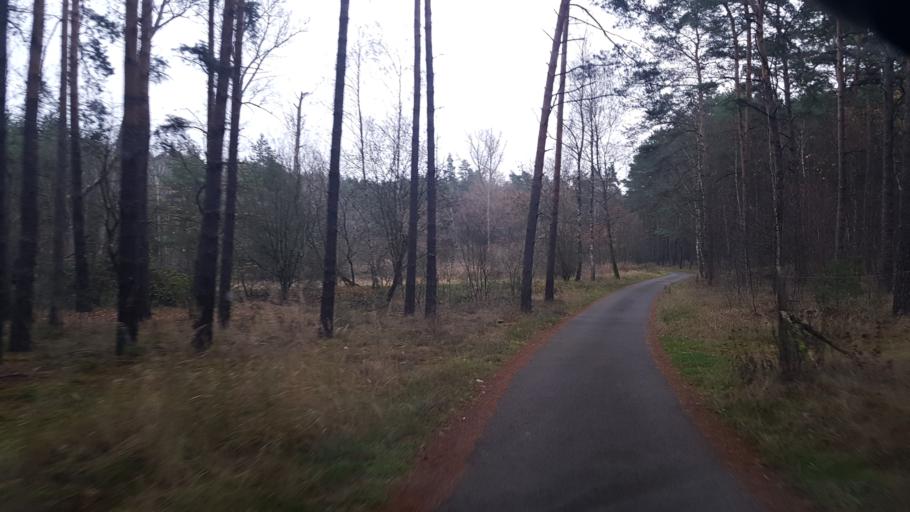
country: DE
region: Brandenburg
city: Schenkendobern
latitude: 51.9803
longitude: 14.6603
